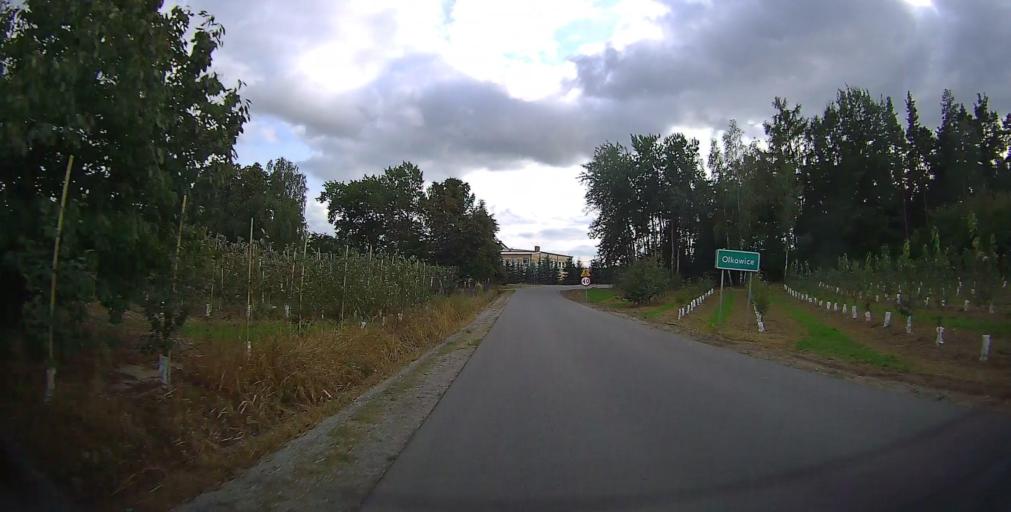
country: PL
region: Masovian Voivodeship
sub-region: Powiat bialobrzeski
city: Promna
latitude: 51.7312
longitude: 20.9647
